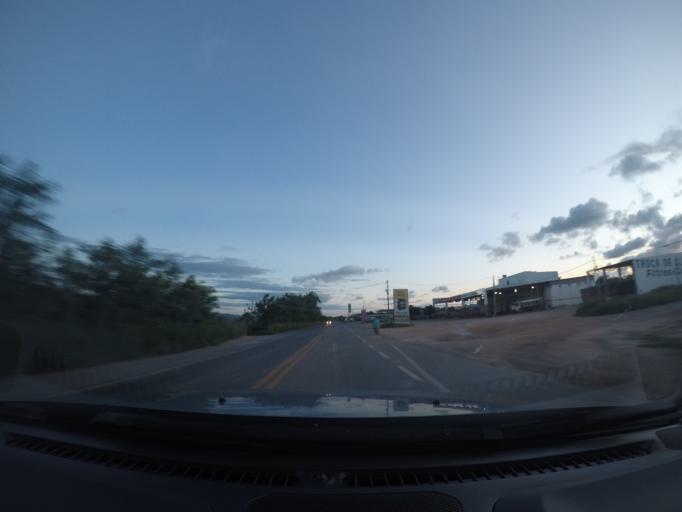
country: BR
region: Bahia
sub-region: Seabra
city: Seabra
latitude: -12.4479
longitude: -41.7514
